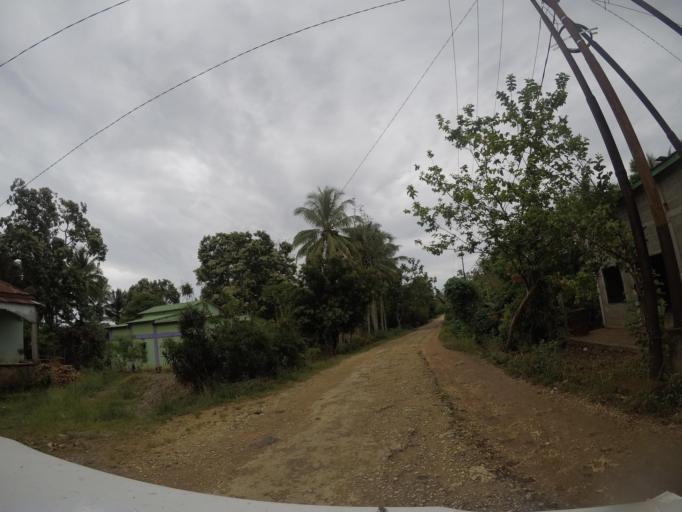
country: TL
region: Lautem
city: Lospalos
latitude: -8.5356
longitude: 126.9966
